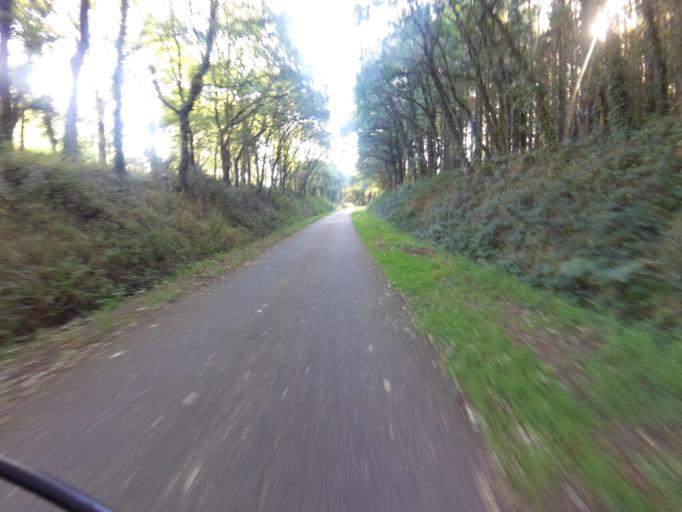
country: FR
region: Brittany
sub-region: Departement du Morbihan
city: Ploermel
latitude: 47.9205
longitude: -2.4255
